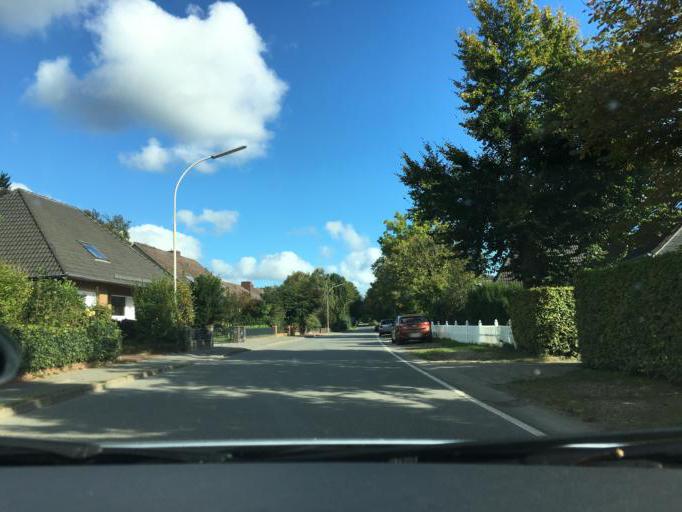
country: DE
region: Schleswig-Holstein
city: Melsdorf
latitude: 54.3190
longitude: 10.0327
